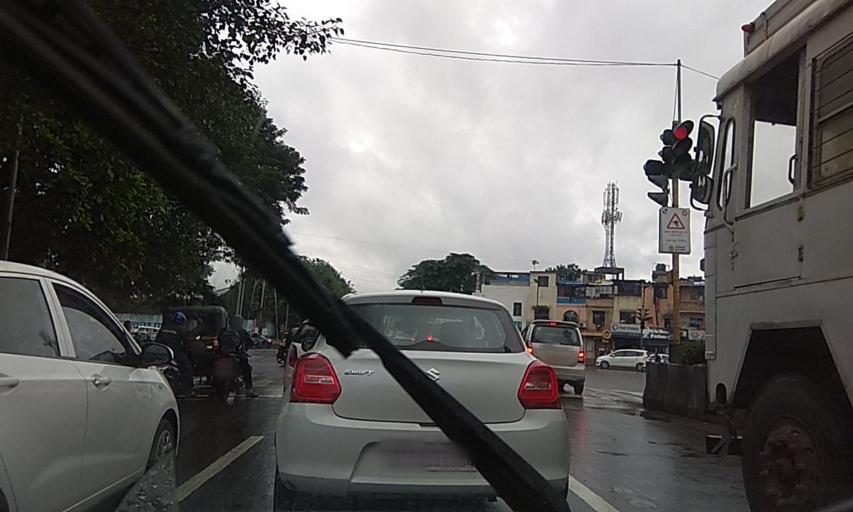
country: IN
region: Maharashtra
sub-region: Pune Division
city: Khadki
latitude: 18.5528
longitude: 73.8791
